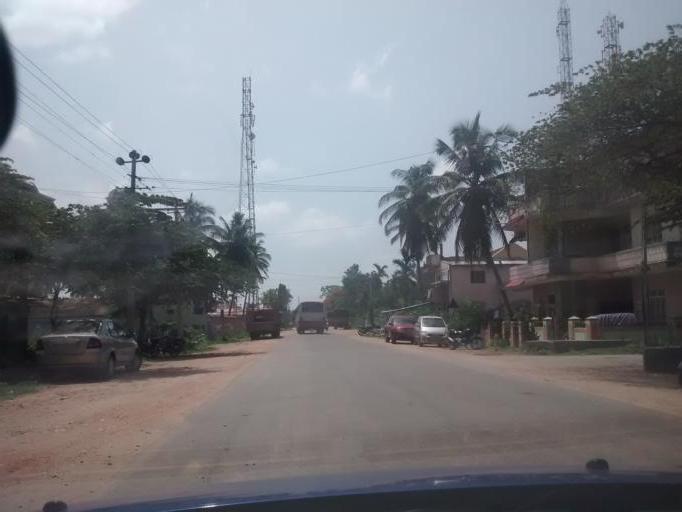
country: IN
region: Karnataka
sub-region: Hassan
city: Konanur
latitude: 12.5632
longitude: 76.2606
